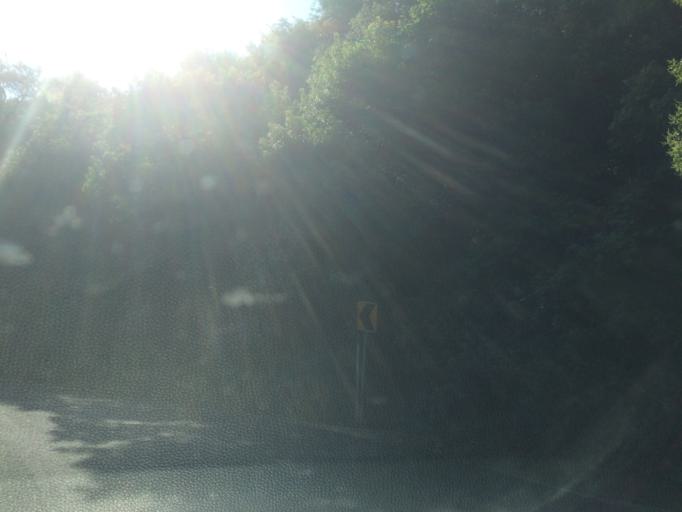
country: MX
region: Nayarit
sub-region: Ahuacatlan
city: Ahuacatlan
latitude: 21.0259
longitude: -104.4758
